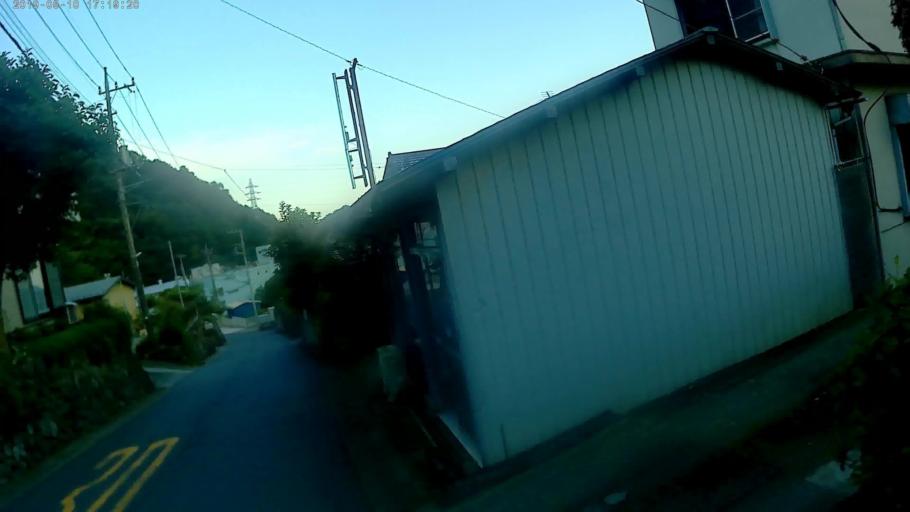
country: JP
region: Yamanashi
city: Uenohara
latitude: 35.6240
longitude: 139.1719
